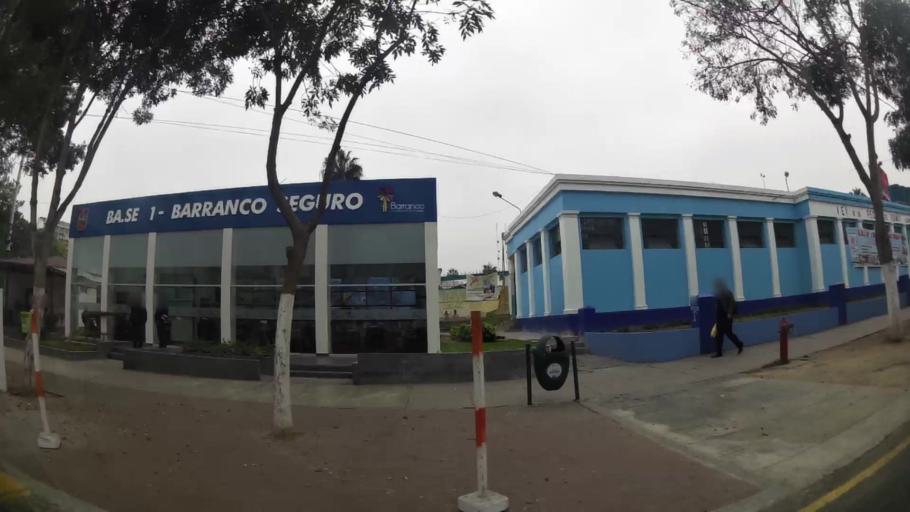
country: PE
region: Lima
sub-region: Lima
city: Surco
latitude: -12.1394
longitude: -77.0234
